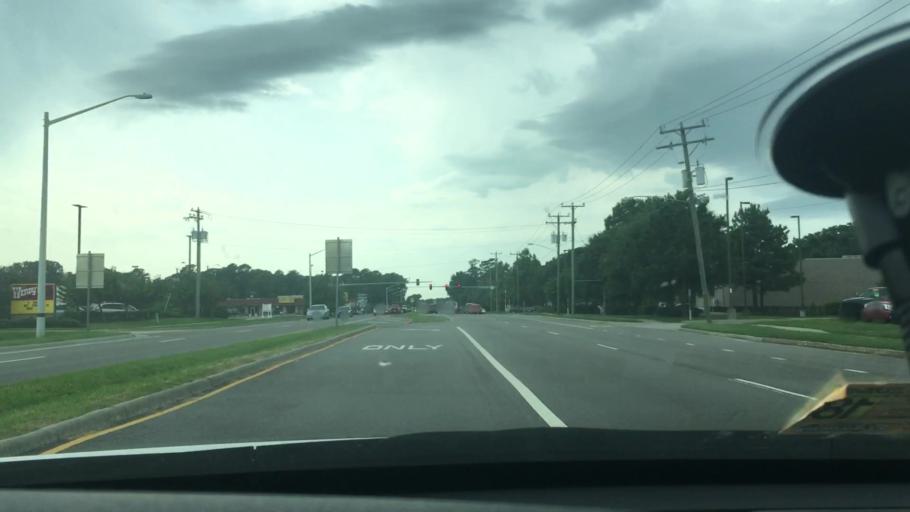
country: US
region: Virginia
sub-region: City of Norfolk
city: Norfolk
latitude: 36.9041
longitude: -76.1335
